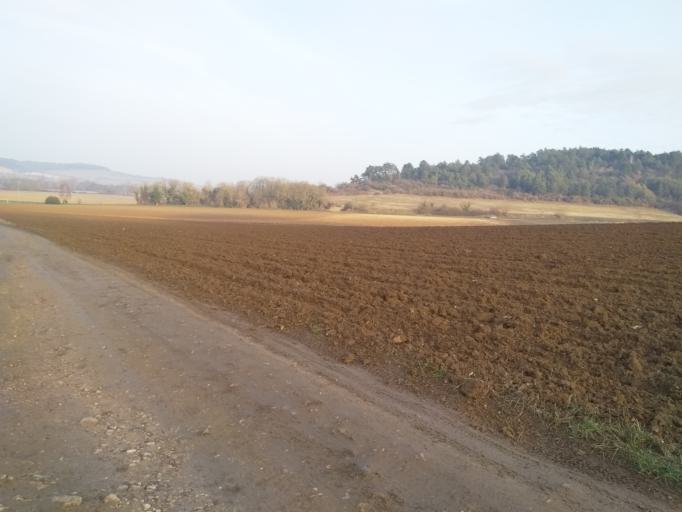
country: FR
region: Bourgogne
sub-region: Departement de l'Yonne
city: Malay-le-Grand
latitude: 48.1658
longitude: 3.3422
